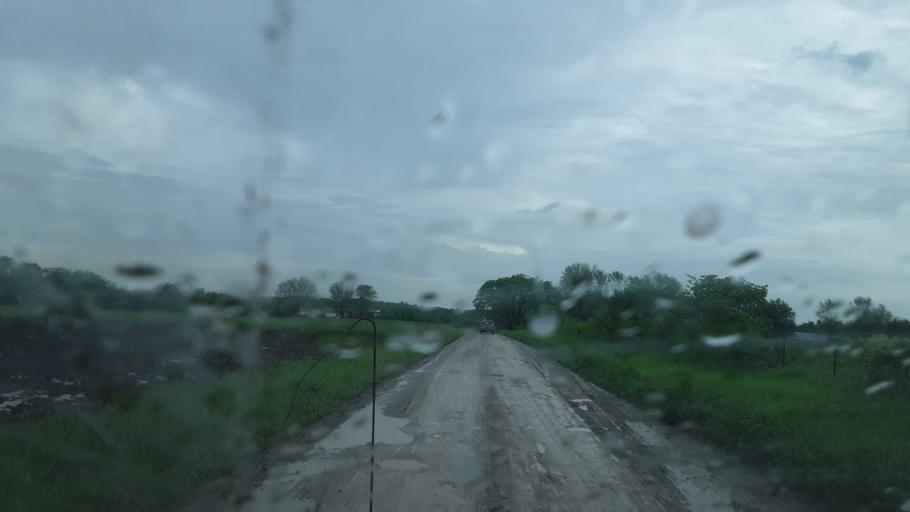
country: US
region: Missouri
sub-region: Clark County
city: Kahoka
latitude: 40.4347
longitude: -91.6157
